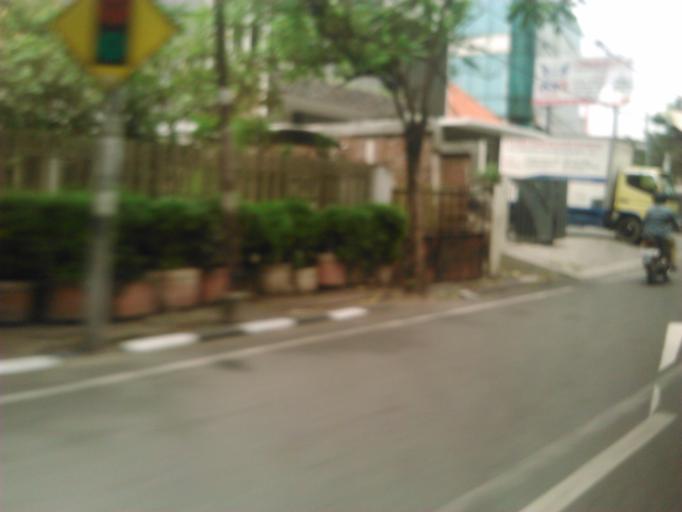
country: ID
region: East Java
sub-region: Kota Surabaya
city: Surabaya
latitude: -7.2632
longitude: 112.7266
